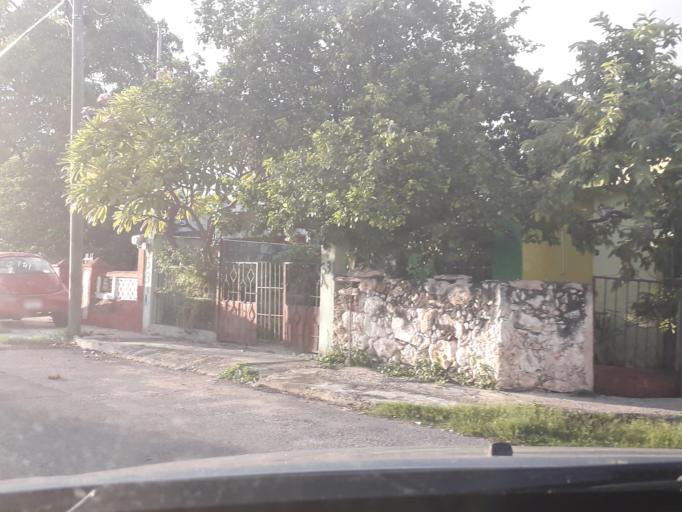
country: MX
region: Yucatan
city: Merida
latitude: 20.9801
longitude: -89.6515
